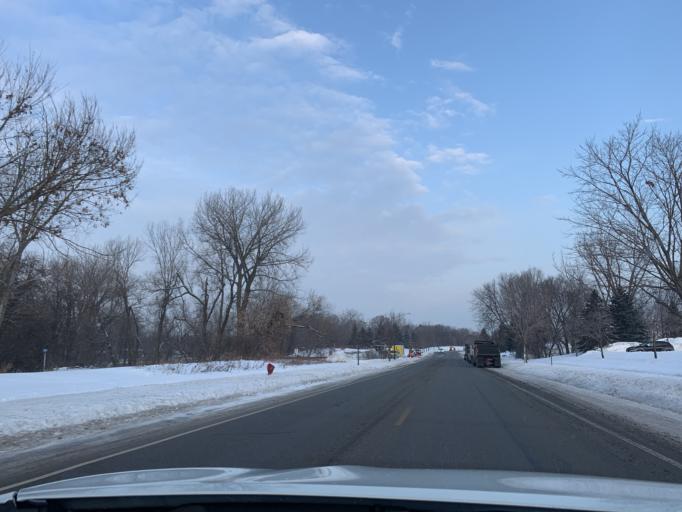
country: US
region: Minnesota
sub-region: Anoka County
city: Coon Rapids
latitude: 45.1575
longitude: -93.2832
